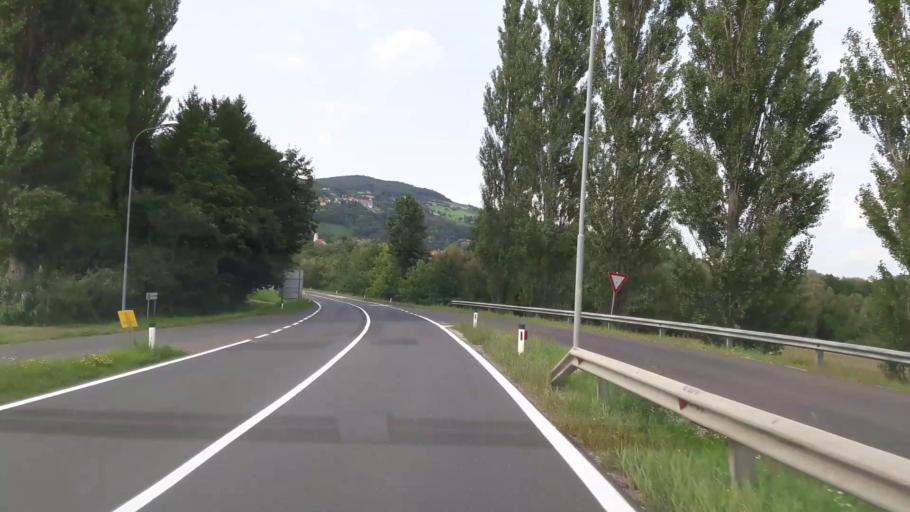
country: AT
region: Styria
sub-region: Politischer Bezirk Hartberg-Fuerstenfeld
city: Hartberg
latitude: 47.2704
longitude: 15.9713
